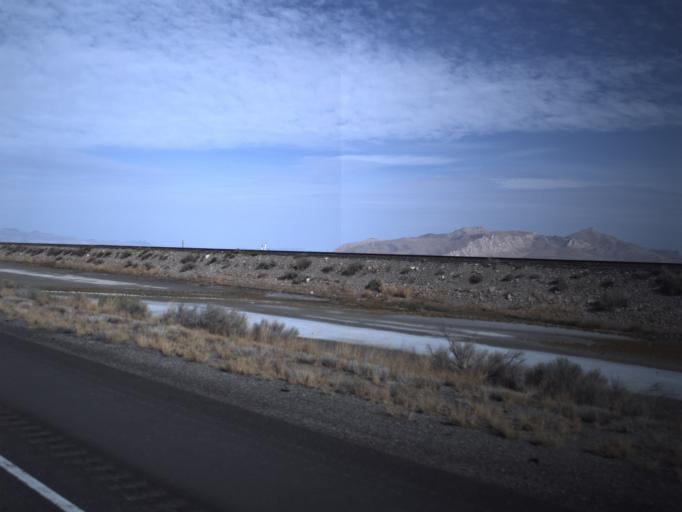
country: US
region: Utah
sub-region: Tooele County
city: Grantsville
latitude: 40.6795
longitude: -112.4145
